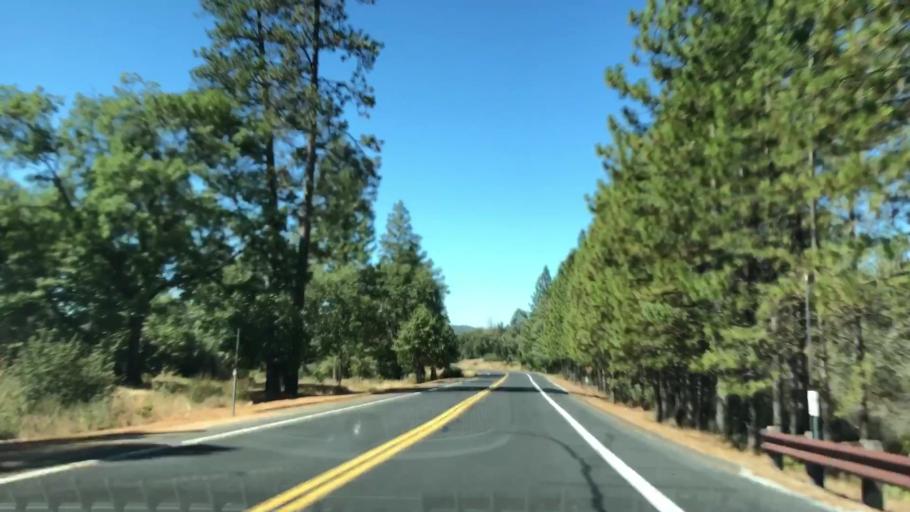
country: US
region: California
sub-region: Tuolumne County
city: Tuolumne City
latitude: 37.8255
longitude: -120.0935
